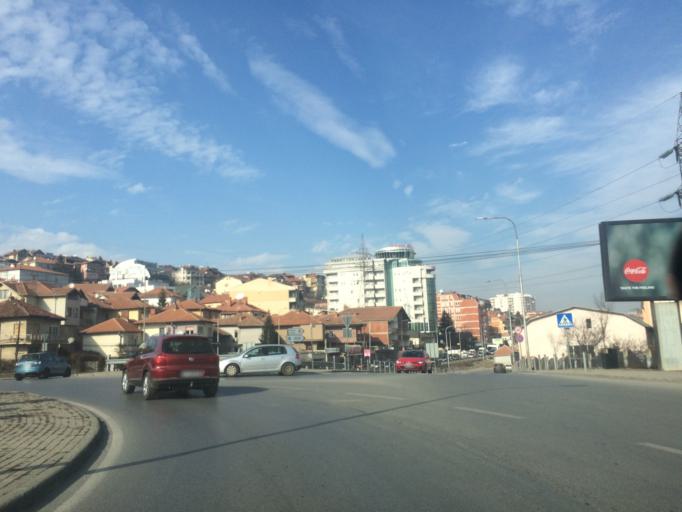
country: XK
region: Pristina
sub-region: Komuna e Prishtines
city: Pristina
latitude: 42.6636
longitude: 21.1552
